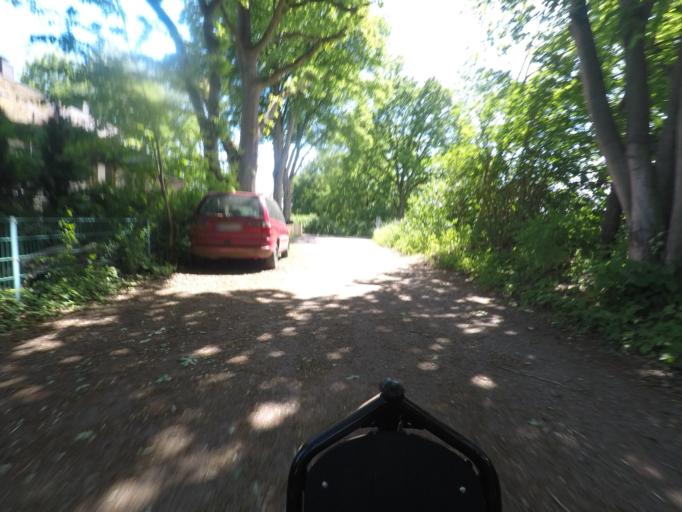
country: DE
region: Schleswig-Holstein
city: Stapelfeld
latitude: 53.6214
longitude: 10.1747
